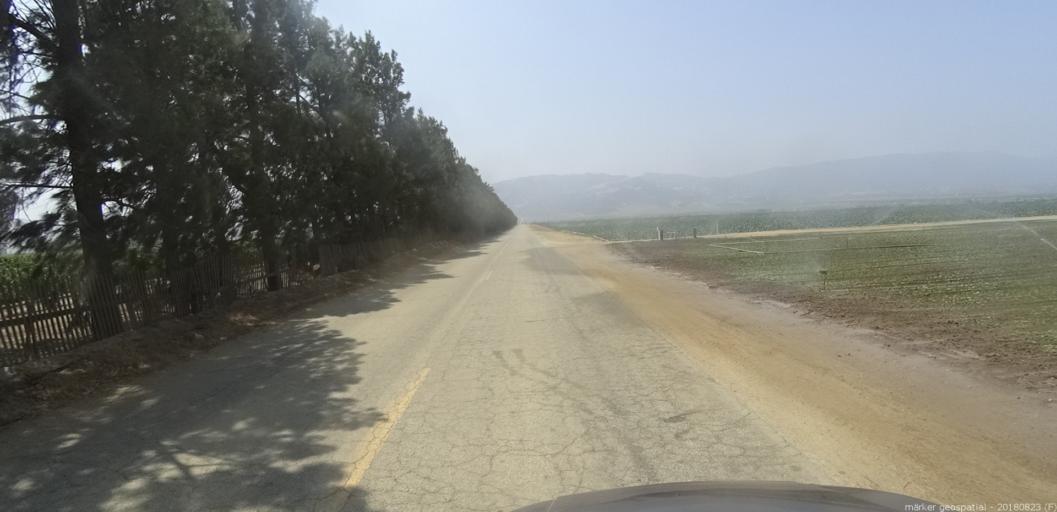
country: US
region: California
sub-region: Monterey County
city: Greenfield
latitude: 36.3321
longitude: -121.2718
